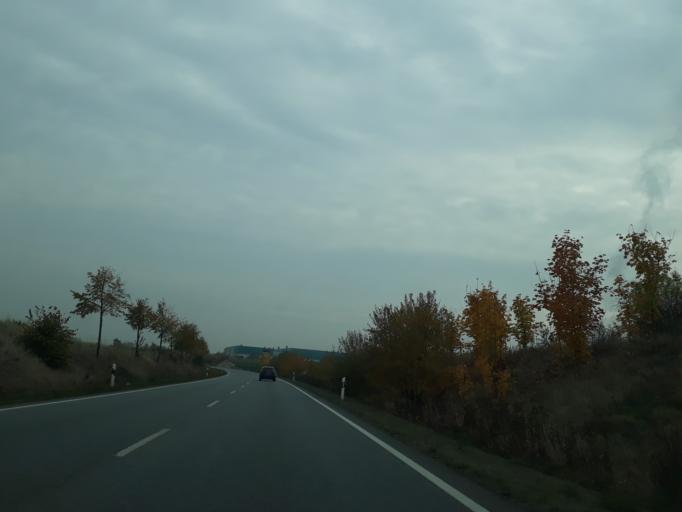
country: DE
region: Saxony
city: Moritzburg
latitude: 51.1319
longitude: 13.7062
